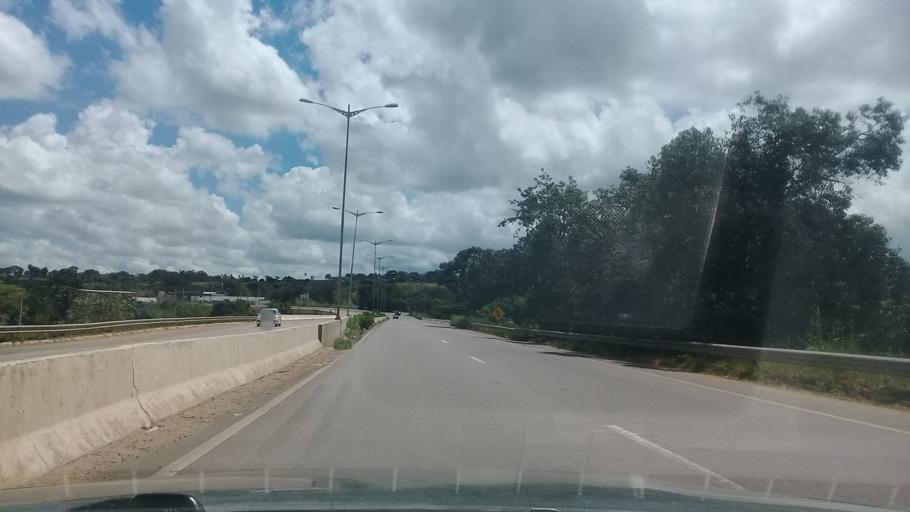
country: BR
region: Pernambuco
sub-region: Carpina
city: Carpina
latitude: -7.8965
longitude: -35.1731
